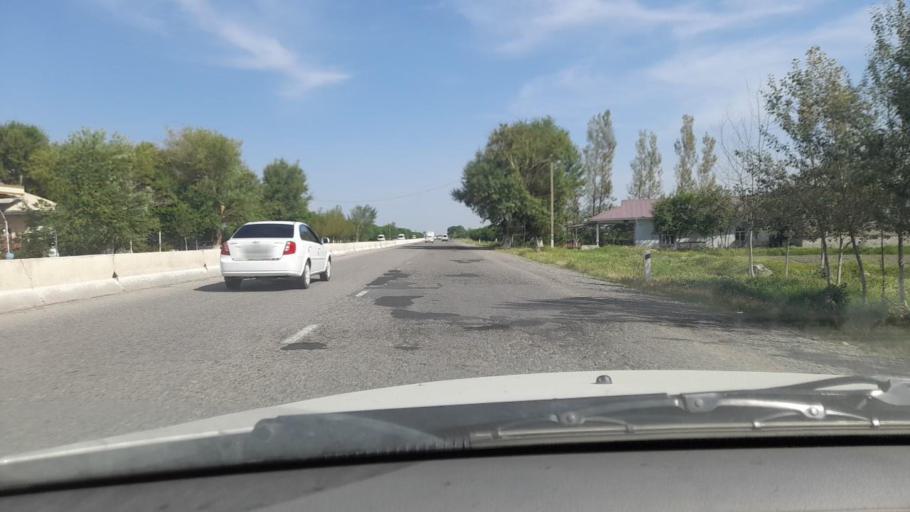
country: UZ
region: Samarqand
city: Chelak
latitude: 39.8468
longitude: 66.8080
